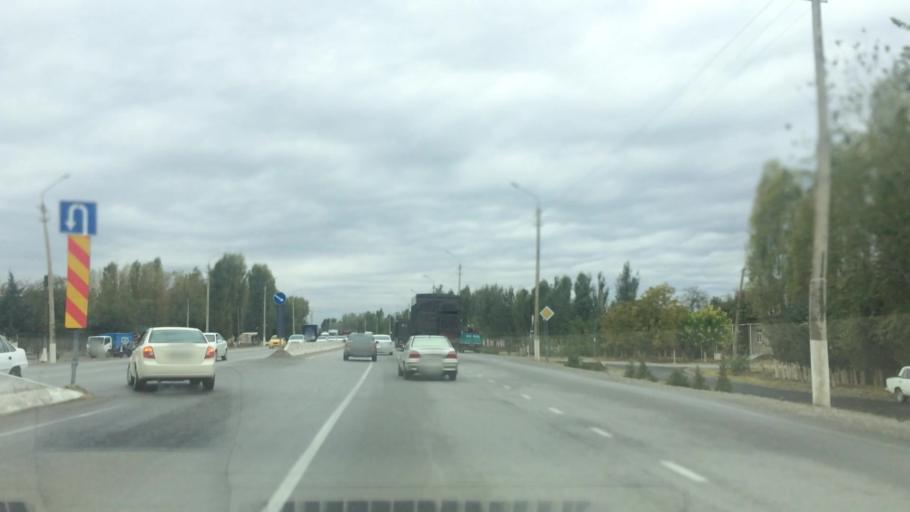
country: UZ
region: Jizzax
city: Jizzax
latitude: 39.9978
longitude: 67.5885
